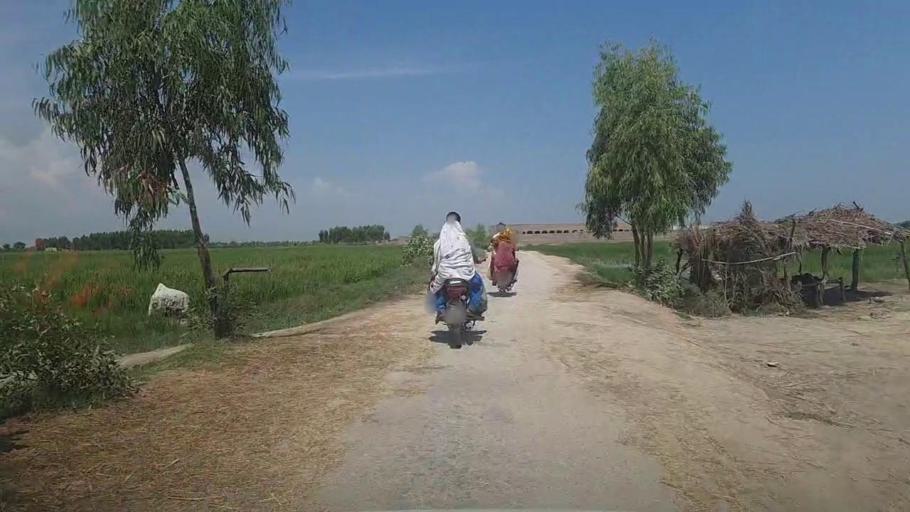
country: PK
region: Sindh
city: Kandhkot
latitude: 28.2867
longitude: 69.2374
